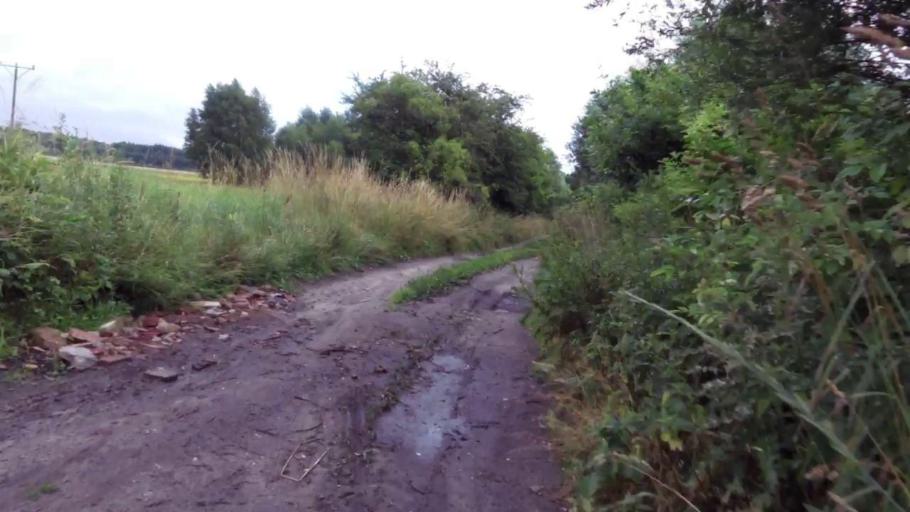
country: PL
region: West Pomeranian Voivodeship
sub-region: Powiat mysliborski
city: Mysliborz
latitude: 52.9645
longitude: 14.8955
